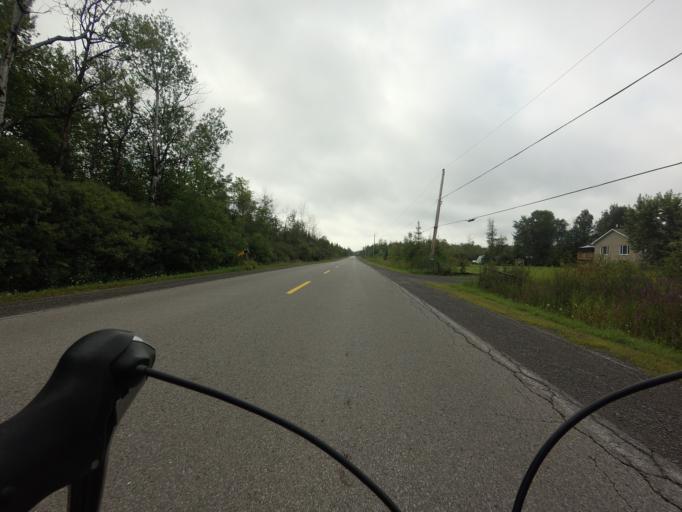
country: CA
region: Ontario
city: Bells Corners
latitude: 45.0752
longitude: -75.7383
